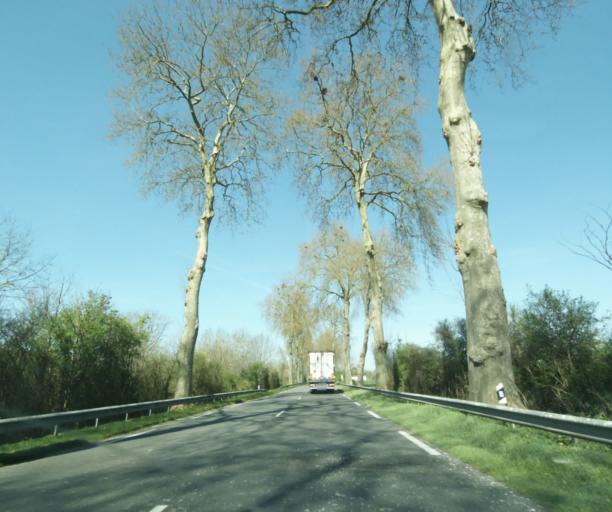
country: FR
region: Bourgogne
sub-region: Departement de la Nievre
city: Chantenay-Saint-Imbert
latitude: 46.7207
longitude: 3.1821
